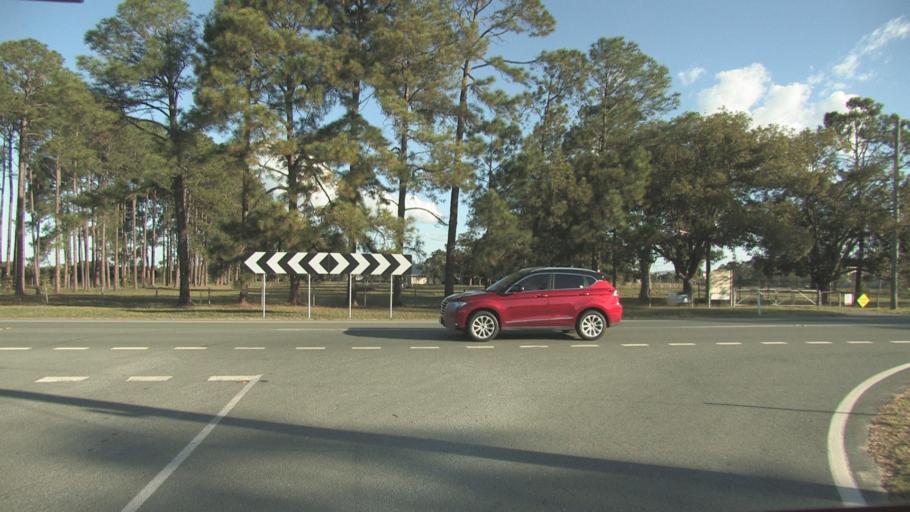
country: AU
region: Queensland
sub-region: Gold Coast
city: Yatala
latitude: -27.6781
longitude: 153.2426
